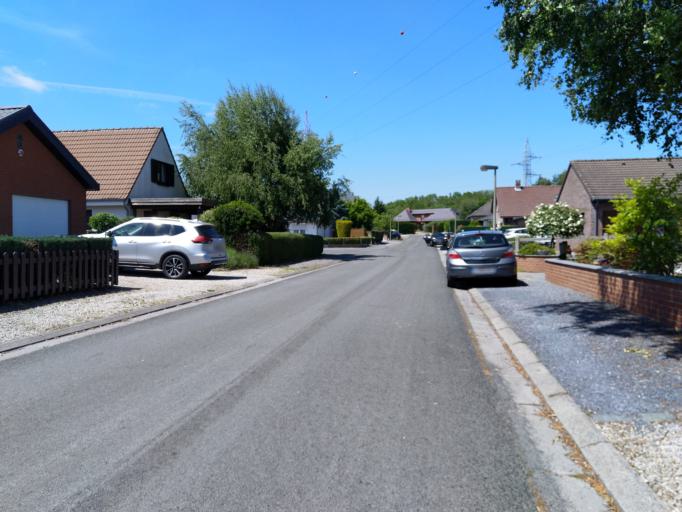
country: BE
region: Wallonia
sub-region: Province du Hainaut
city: Saint-Ghislain
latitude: 50.4733
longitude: 3.8196
